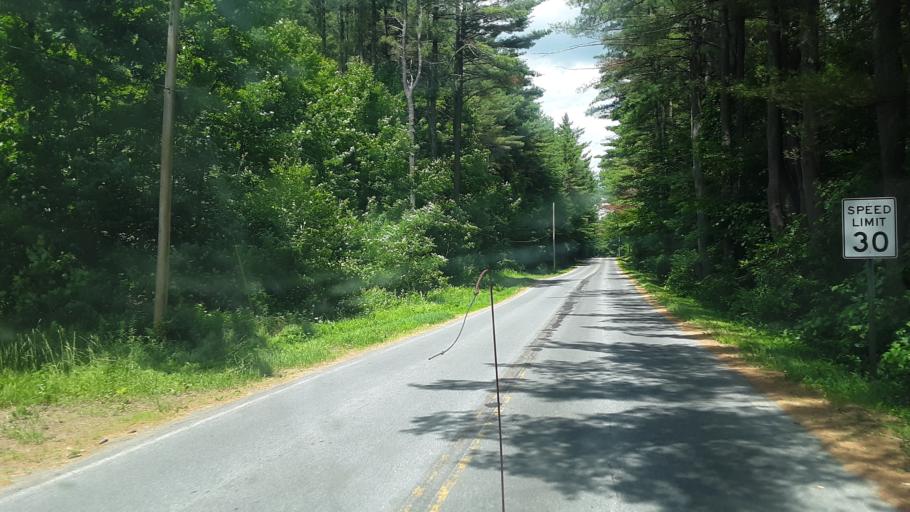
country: US
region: New York
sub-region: Oneida County
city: Rome
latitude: 43.2526
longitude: -75.5966
